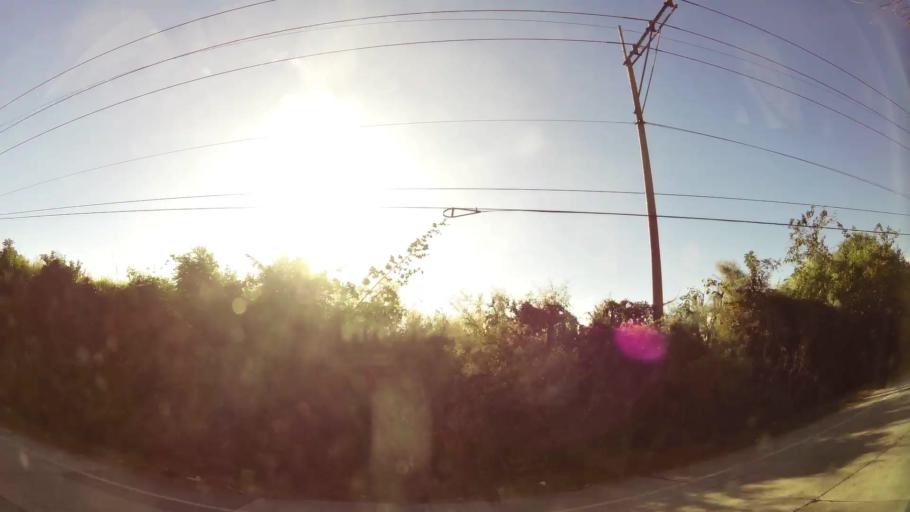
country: SV
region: Santa Ana
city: Metapan
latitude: 14.2561
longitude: -89.4608
